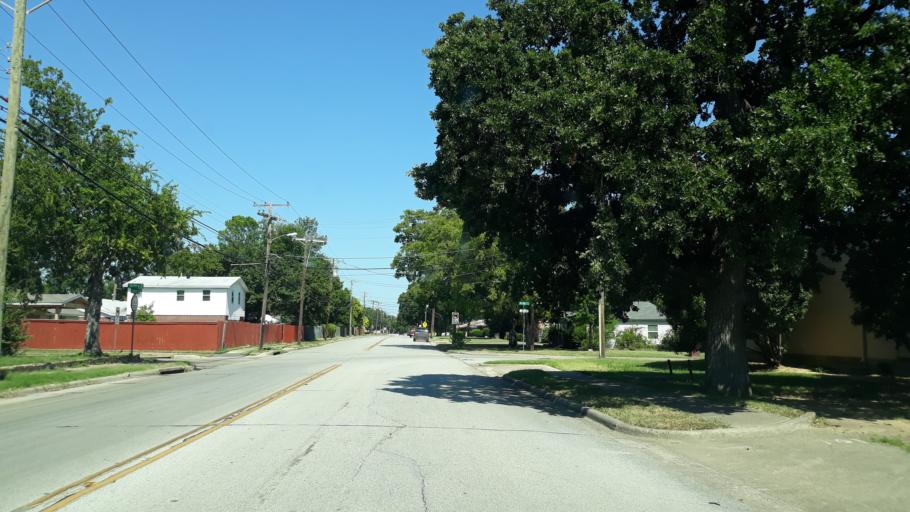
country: US
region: Texas
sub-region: Dallas County
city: Irving
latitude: 32.8218
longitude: -96.9899
